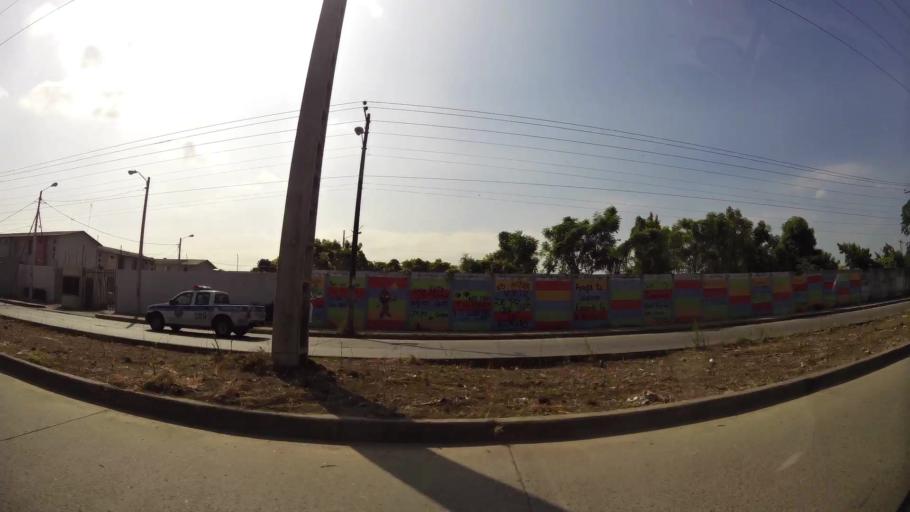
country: EC
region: Guayas
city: Eloy Alfaro
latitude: -2.1667
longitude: -79.8064
